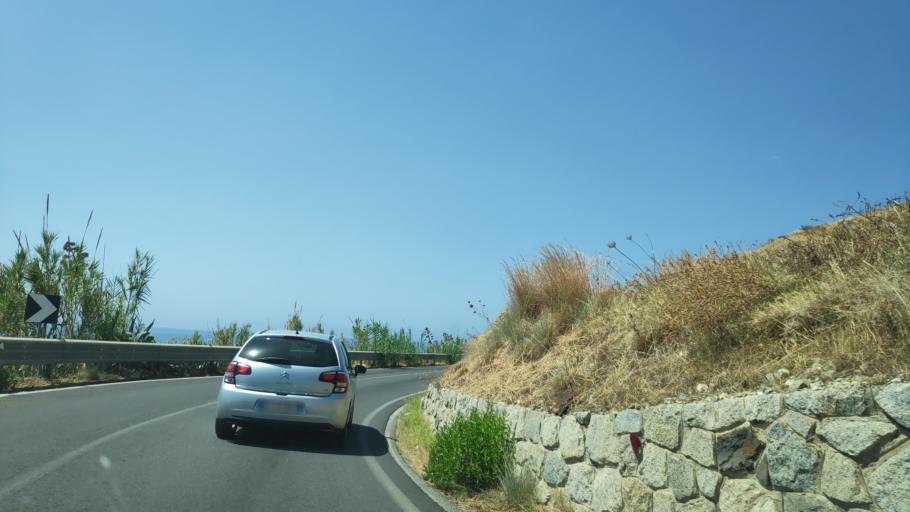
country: IT
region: Calabria
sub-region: Provincia di Reggio Calabria
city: Palizzi Marina
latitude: 37.9168
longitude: 15.9989
